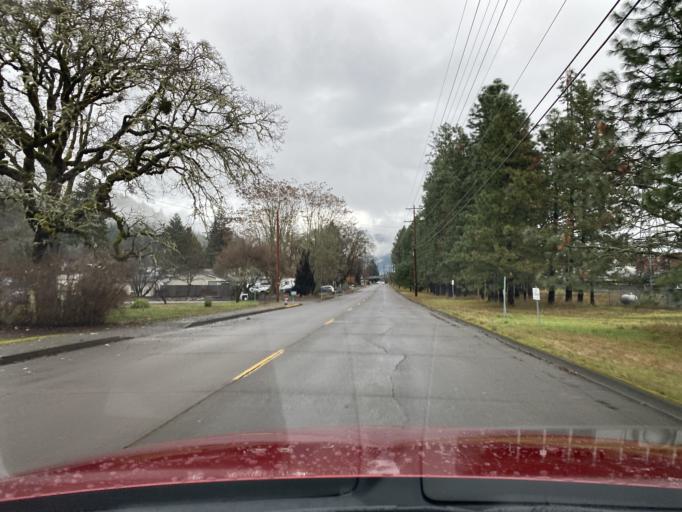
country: US
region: Oregon
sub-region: Lane County
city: Oakridge
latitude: 43.7473
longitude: -122.4732
